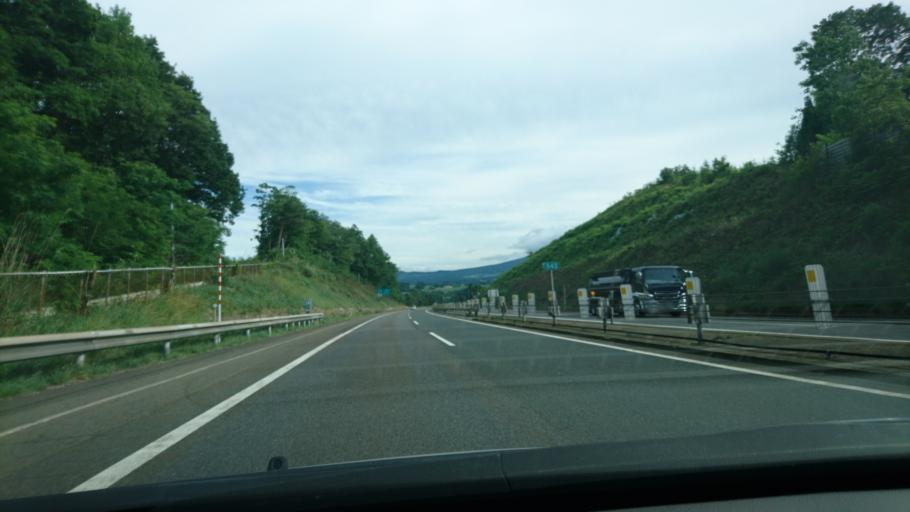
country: JP
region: Iwate
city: Shizukuishi
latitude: 39.9622
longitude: 141.0317
